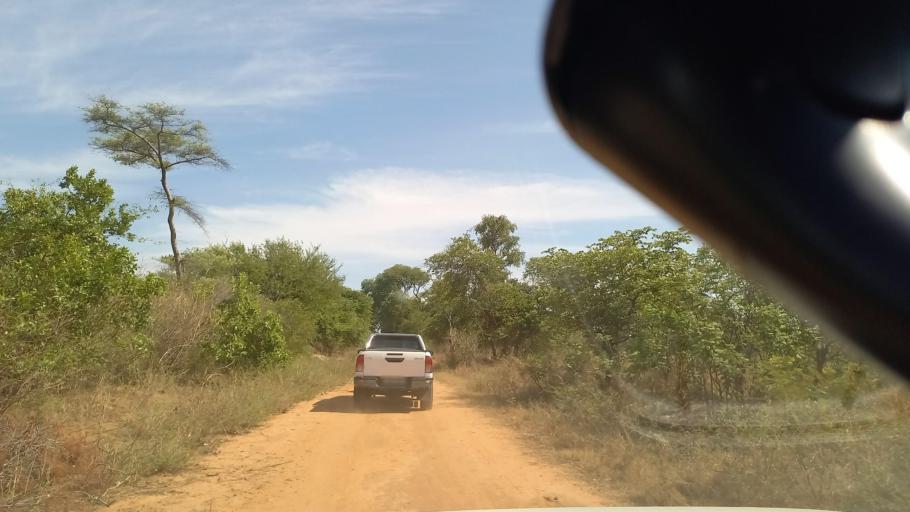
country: ZM
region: Southern
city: Mazabuka
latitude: -16.0370
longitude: 27.6226
